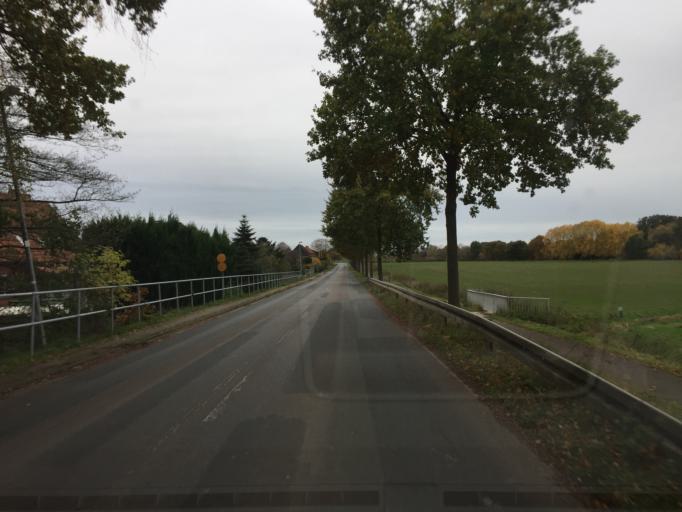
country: DE
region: Lower Saxony
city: Linsburg
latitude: 52.5932
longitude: 9.3021
